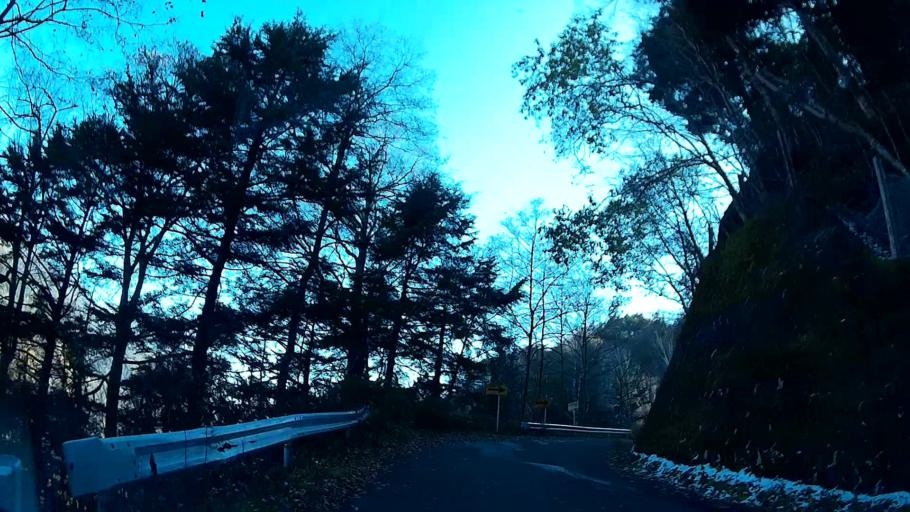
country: JP
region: Nagano
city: Hotaka
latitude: 36.2059
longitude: 137.5991
